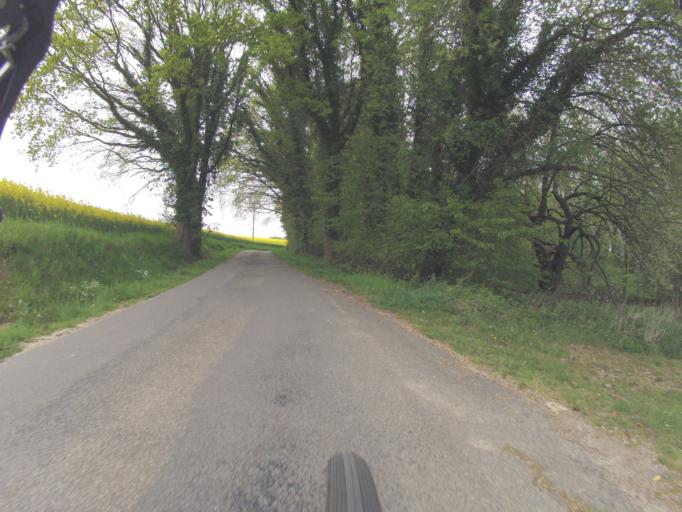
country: DE
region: North Rhine-Westphalia
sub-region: Regierungsbezirk Munster
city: Westerkappeln
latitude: 52.2959
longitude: 7.8409
